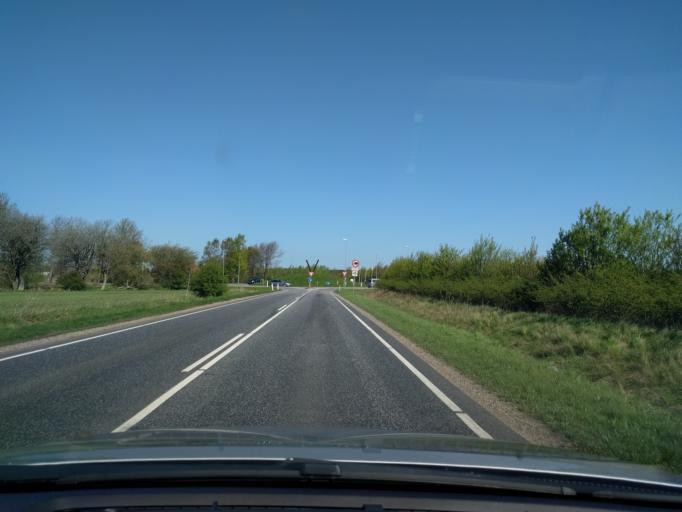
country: DK
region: Central Jutland
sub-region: Ringkobing-Skjern Kommune
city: Videbaek
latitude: 56.0916
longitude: 8.6493
